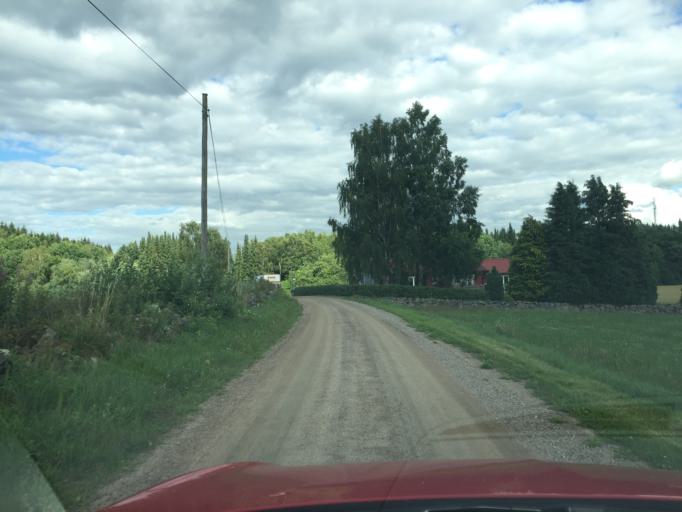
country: SE
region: Skane
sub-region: Hassleholms Kommun
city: Sosdala
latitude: 56.0473
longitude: 13.6903
